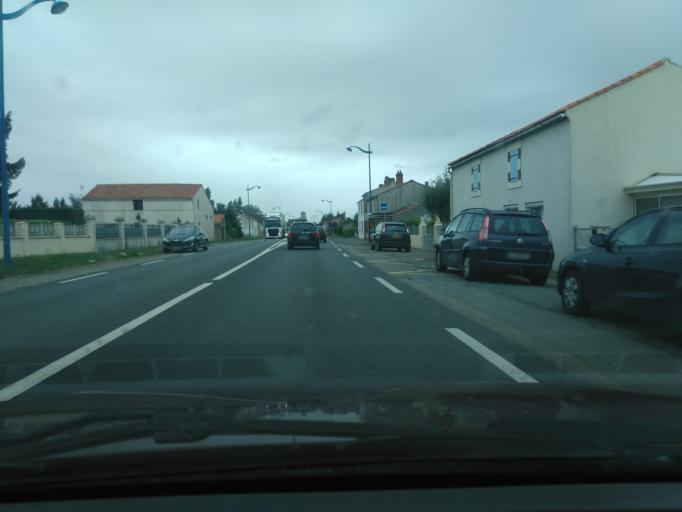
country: FR
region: Pays de la Loire
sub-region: Departement de la Vendee
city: Sainte-Gemme-la-Plaine
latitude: 46.4741
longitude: -1.1108
